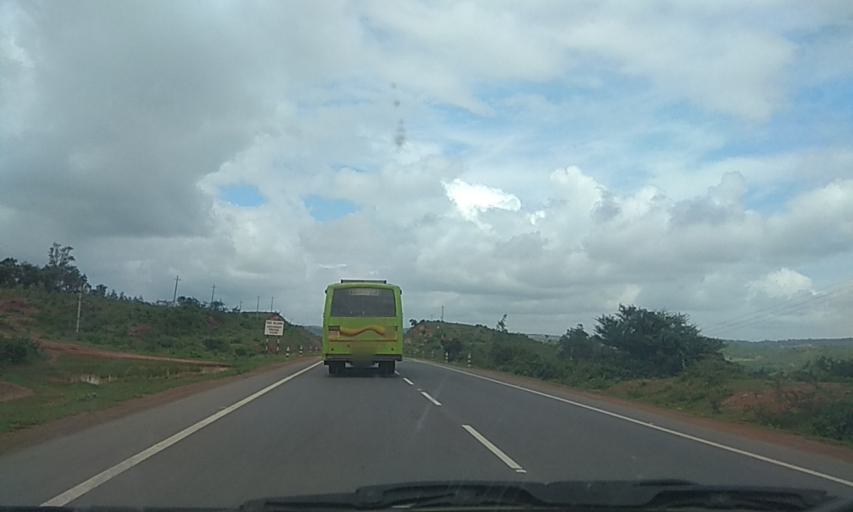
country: IN
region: Karnataka
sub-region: Dharwad
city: Hubli
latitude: 15.4007
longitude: 74.9986
